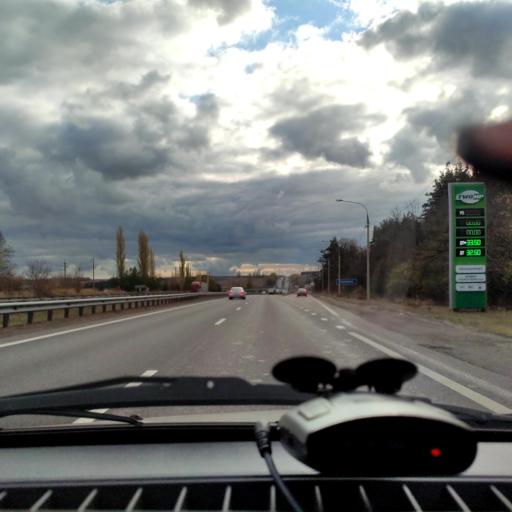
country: RU
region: Voronezj
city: Ramon'
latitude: 51.9497
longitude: 39.2218
